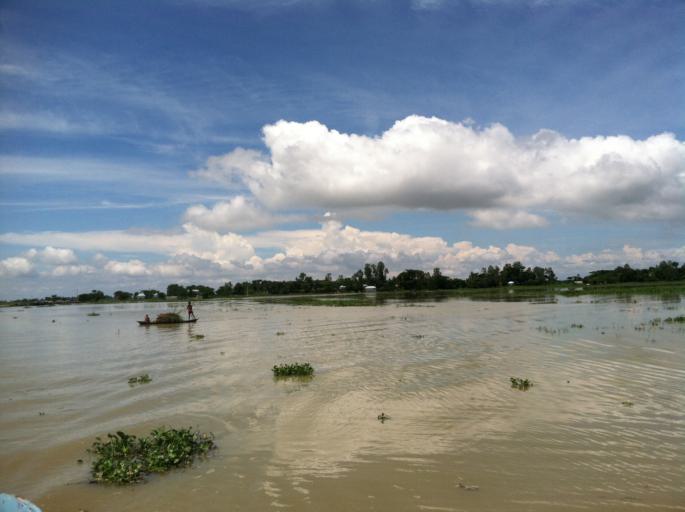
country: BD
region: Sylhet
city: Baniachang
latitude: 24.6411
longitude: 91.3348
